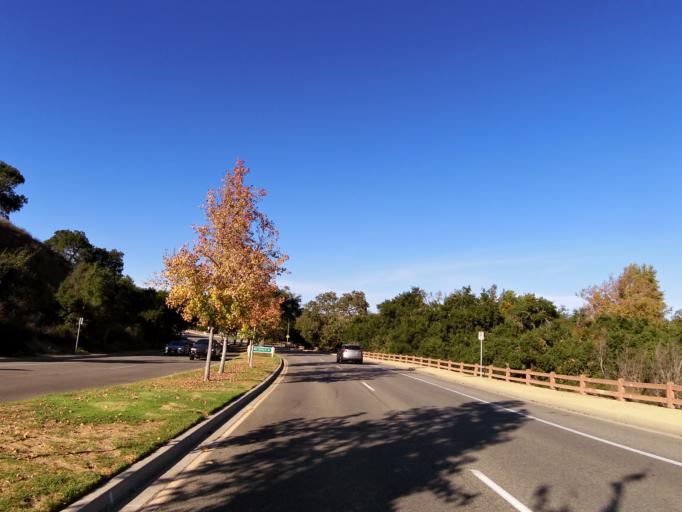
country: US
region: California
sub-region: Ventura County
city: Thousand Oaks
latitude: 34.1870
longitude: -118.8217
